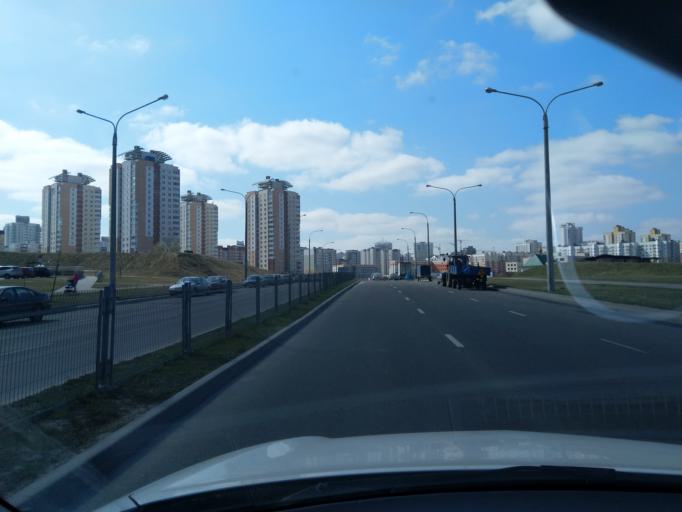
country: BY
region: Minsk
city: Yubilyeyny
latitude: 53.8525
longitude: 27.4903
